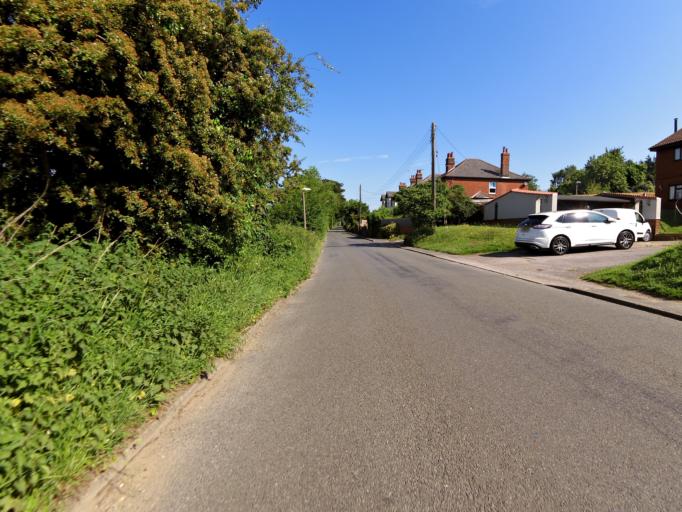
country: GB
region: England
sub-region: Suffolk
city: Bramford
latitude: 52.0789
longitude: 1.1061
